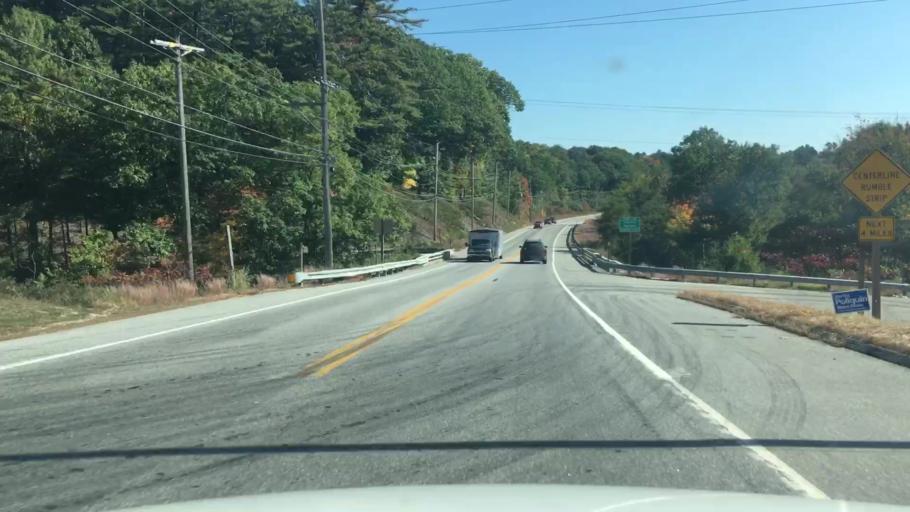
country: US
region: Maine
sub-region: Androscoggin County
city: Lisbon Falls
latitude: 43.9931
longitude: -70.0517
